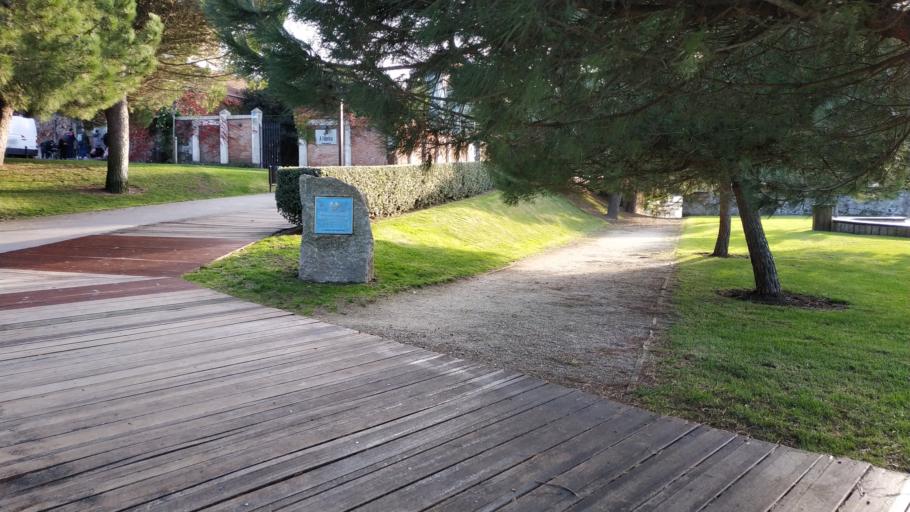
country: ES
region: Galicia
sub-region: Provincia da Coruna
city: A Coruna
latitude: 43.3360
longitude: -8.3800
